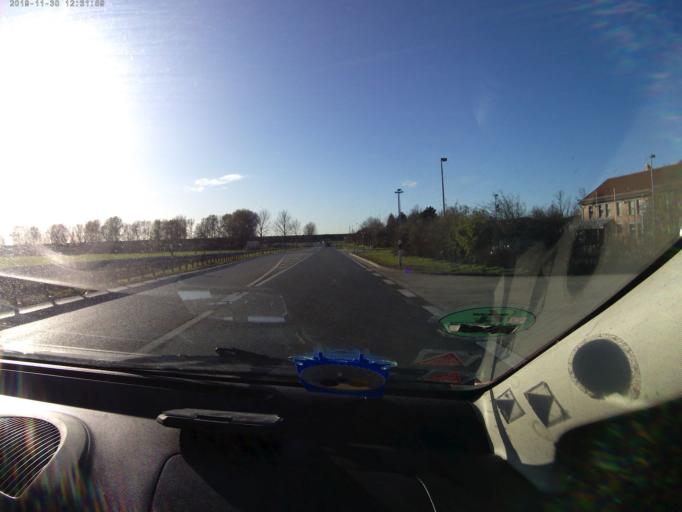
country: DE
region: Lower Saxony
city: Jemgum
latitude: 53.2370
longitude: 7.4133
